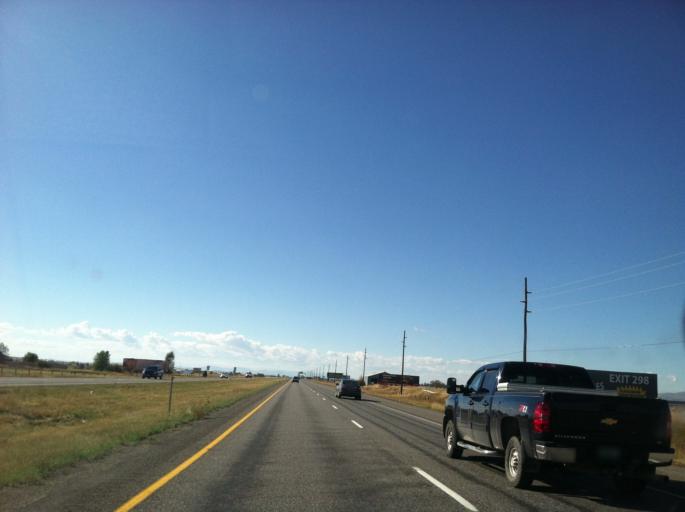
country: US
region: Montana
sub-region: Gallatin County
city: Belgrade
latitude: 45.7531
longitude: -111.1415
